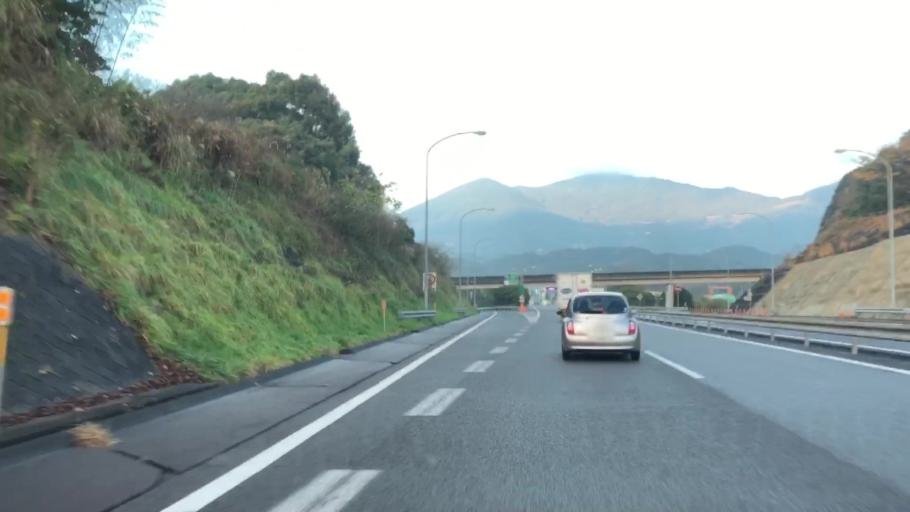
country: JP
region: Saga Prefecture
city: Imaricho-ko
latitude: 33.1692
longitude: 129.8518
